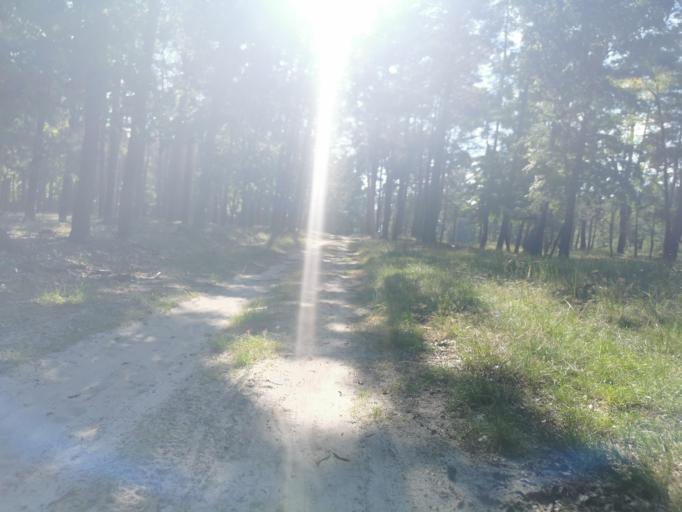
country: SK
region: Trnavsky
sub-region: Okres Senica
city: Senica
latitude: 48.6027
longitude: 17.2633
